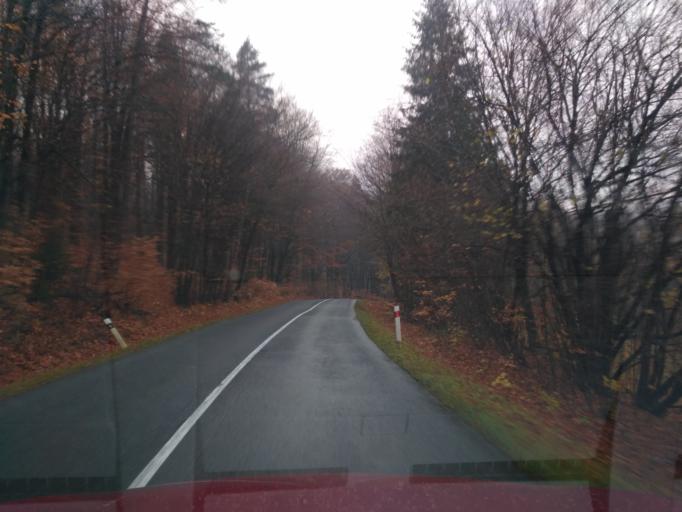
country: SK
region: Kosicky
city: Medzev
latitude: 48.7033
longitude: 20.8307
